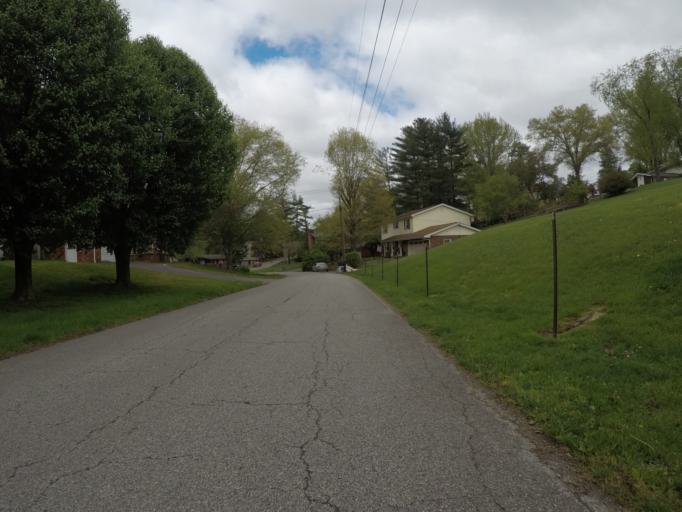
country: US
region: West Virginia
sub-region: Cabell County
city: Pea Ridge
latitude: 38.4084
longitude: -82.3360
